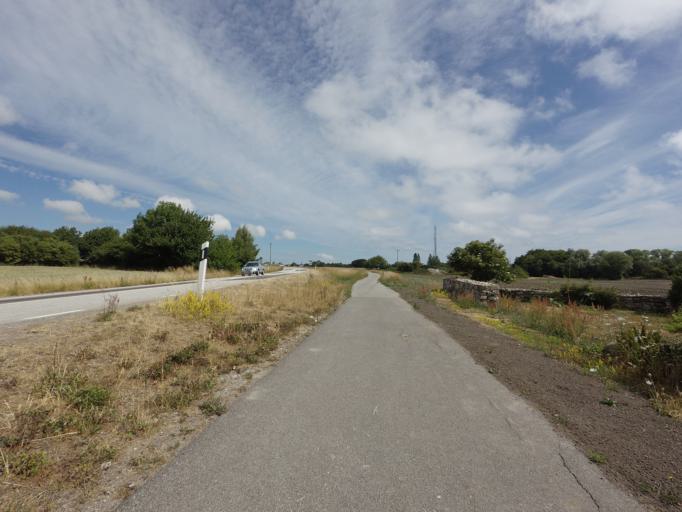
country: SE
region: Skane
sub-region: Simrishamns Kommun
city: Simrishamn
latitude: 55.5093
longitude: 14.3355
